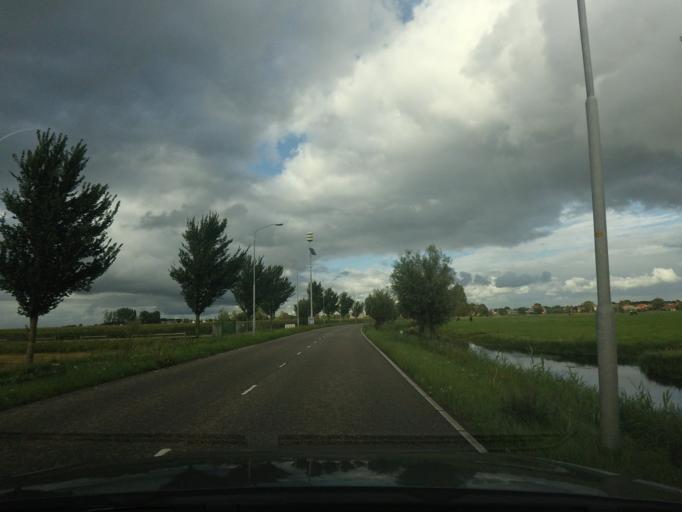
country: NL
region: North Holland
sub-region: Gemeente Heemskerk
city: Heemskerk
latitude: 52.5123
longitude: 4.6941
